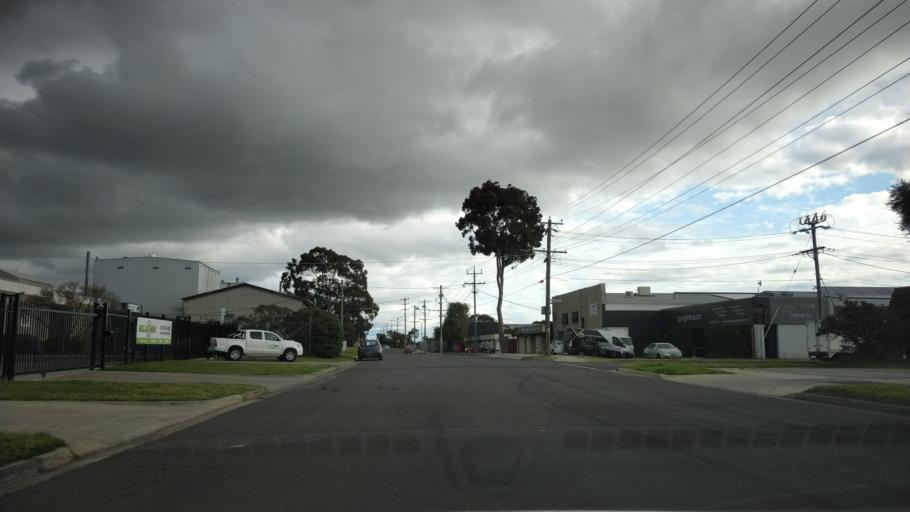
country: AU
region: Victoria
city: Highett
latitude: -37.9523
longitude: 145.0736
